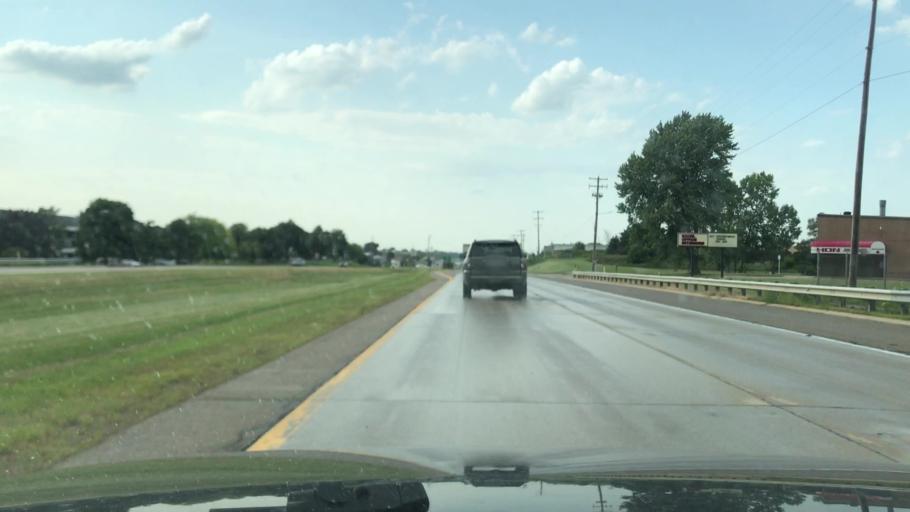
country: US
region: Michigan
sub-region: Kent County
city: East Grand Rapids
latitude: 42.8800
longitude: -85.5622
